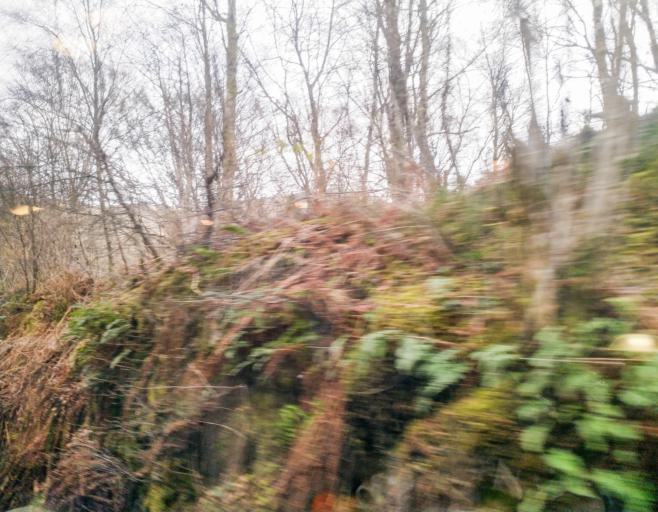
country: GB
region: Scotland
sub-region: Argyll and Bute
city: Garelochhead
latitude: 56.3615
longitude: -4.6735
